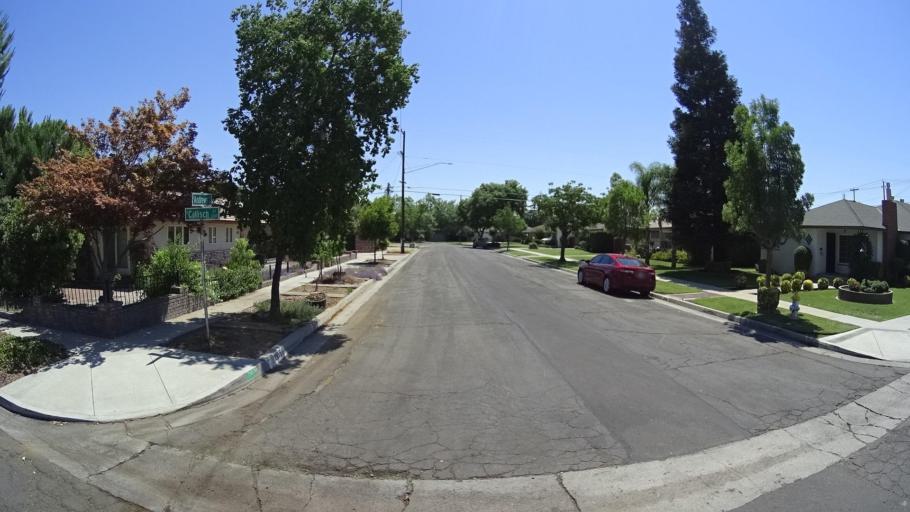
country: US
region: California
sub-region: Fresno County
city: Fresno
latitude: 36.7806
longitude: -119.7765
